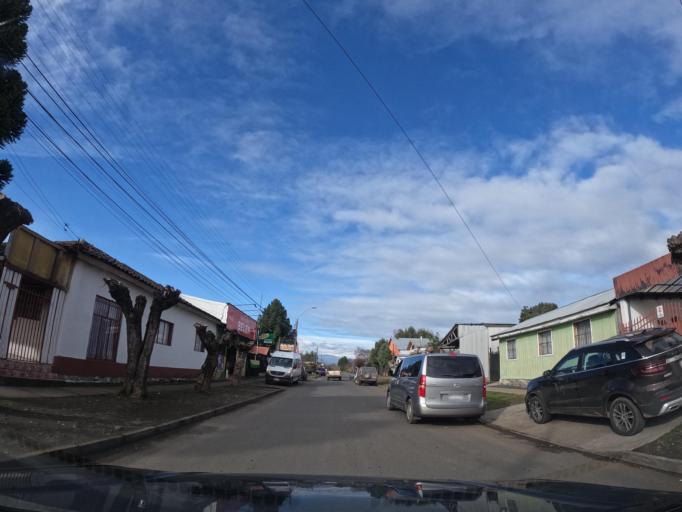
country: CL
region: Biobio
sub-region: Provincia de Nuble
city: Coihueco
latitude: -36.7033
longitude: -71.8910
